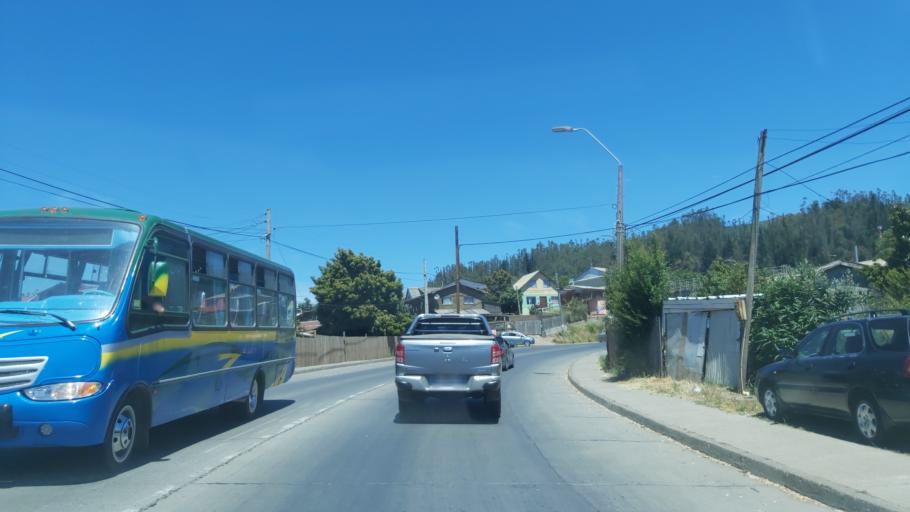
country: CL
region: Maule
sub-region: Provincia de Talca
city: Constitucion
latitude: -35.3420
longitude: -72.4174
